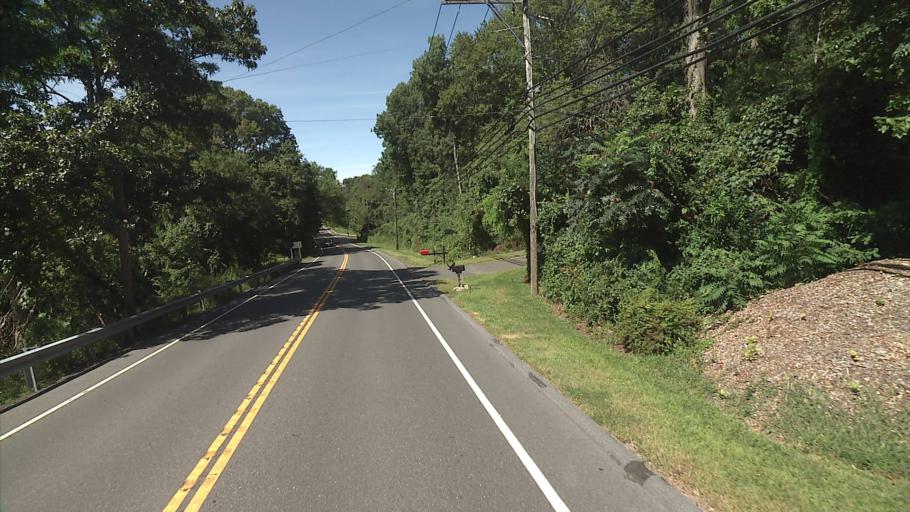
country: US
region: Connecticut
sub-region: New Haven County
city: Oxford
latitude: 41.4070
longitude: -73.1429
